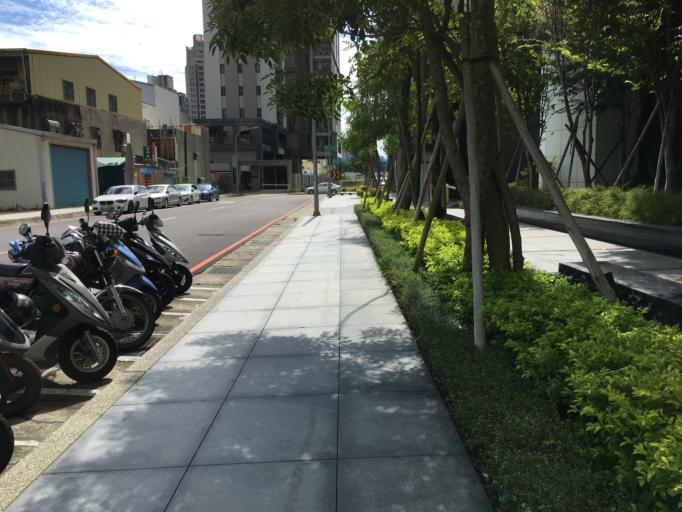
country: TW
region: Taiwan
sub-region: Hsinchu
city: Zhubei
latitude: 24.7908
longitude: 121.0152
